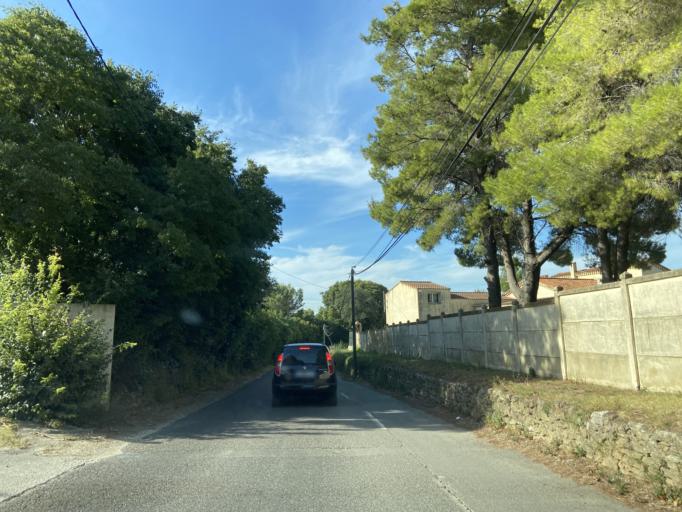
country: FR
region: Provence-Alpes-Cote d'Azur
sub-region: Departement des Bouches-du-Rhone
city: Miramas
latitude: 43.5694
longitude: 5.0193
